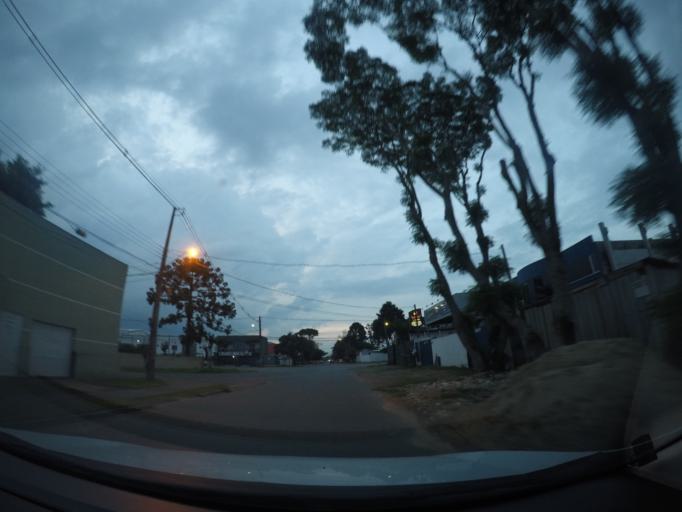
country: BR
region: Parana
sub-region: Sao Jose Dos Pinhais
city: Sao Jose dos Pinhais
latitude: -25.5044
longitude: -49.2278
